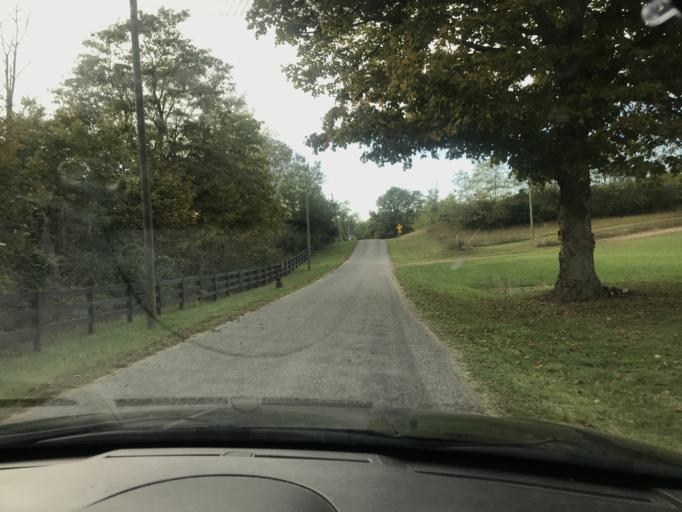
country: US
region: Ohio
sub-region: Logan County
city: West Liberty
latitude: 40.2256
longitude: -83.6645
